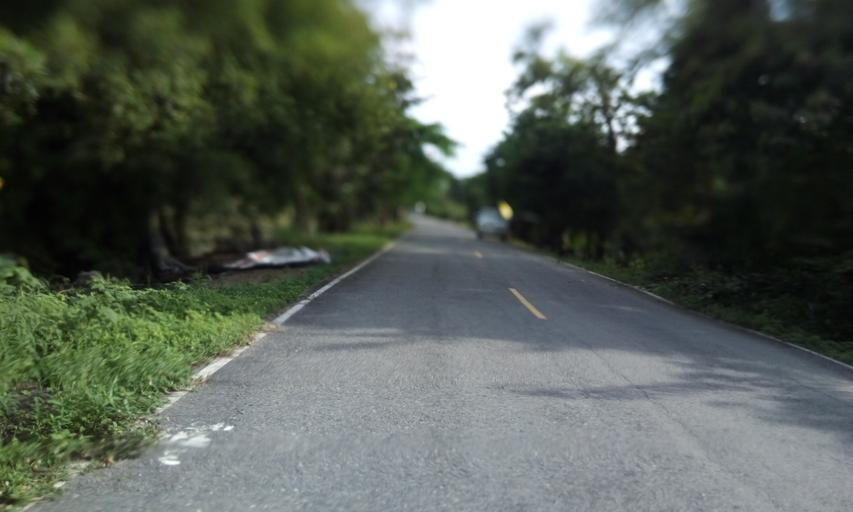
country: TH
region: Pathum Thani
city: Nong Suea
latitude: 14.0841
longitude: 100.8237
